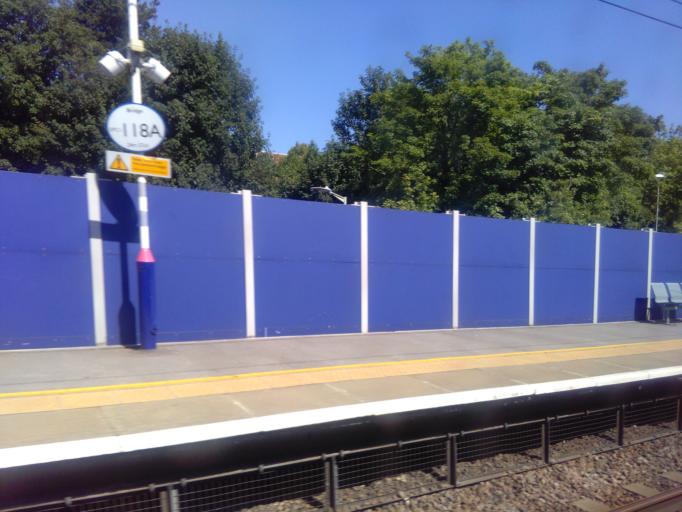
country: GB
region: England
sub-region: Hertfordshire
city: Harpenden
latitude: 51.8157
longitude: -0.3520
